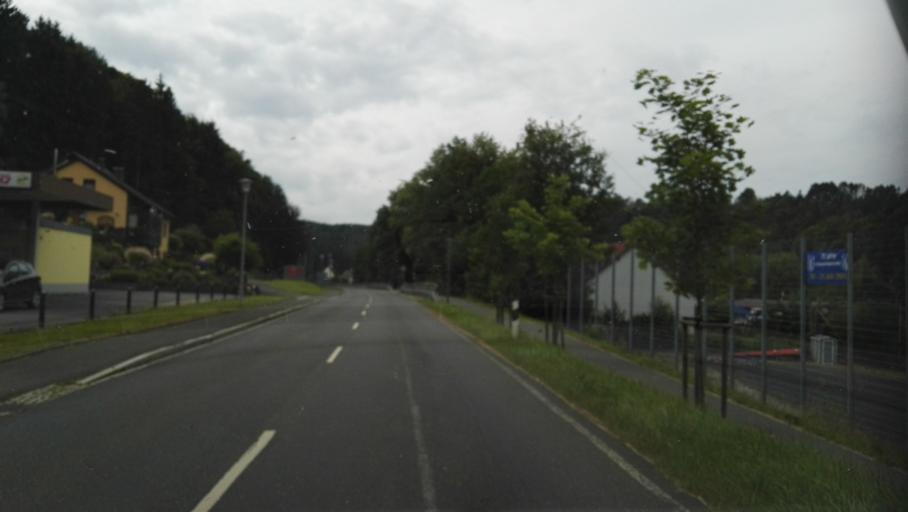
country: DE
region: Bavaria
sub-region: Upper Franconia
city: Waischenfeld
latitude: 49.8498
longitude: 11.3424
